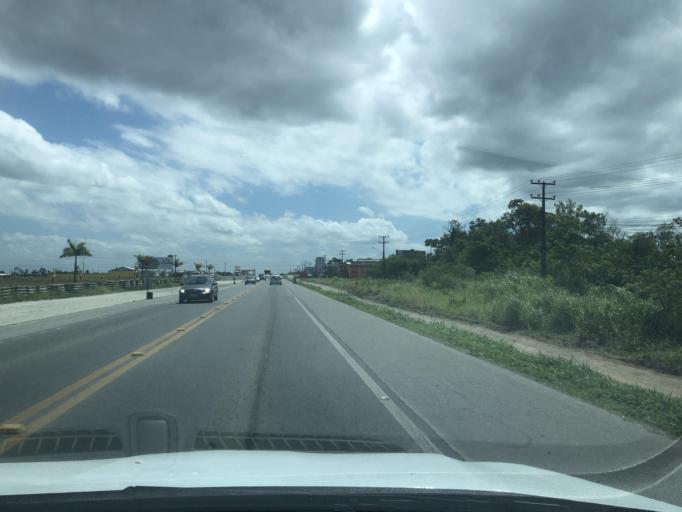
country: BR
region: Santa Catarina
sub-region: Joinville
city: Joinville
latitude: -26.3835
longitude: -48.7268
